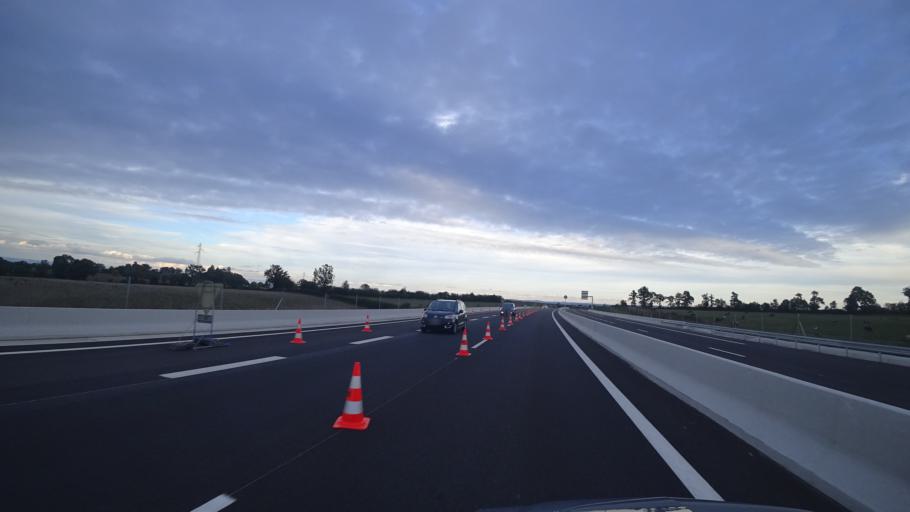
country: FR
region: Midi-Pyrenees
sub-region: Departement de l'Aveyron
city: Luc-la-Primaube
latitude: 44.2911
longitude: 2.5038
